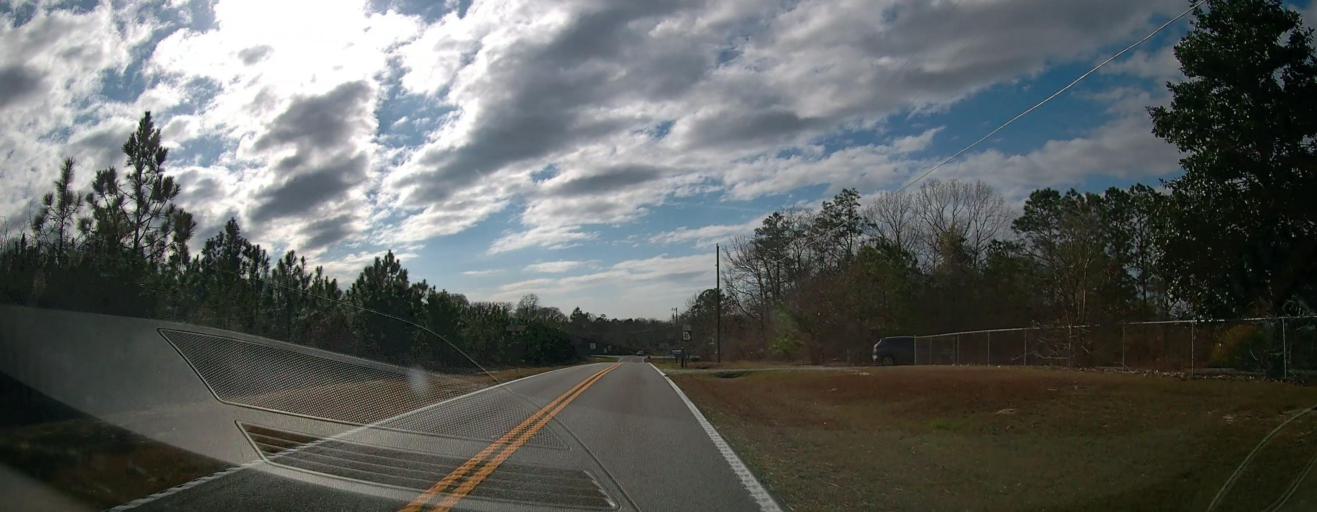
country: US
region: Georgia
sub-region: Marion County
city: Buena Vista
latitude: 32.4446
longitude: -84.5344
